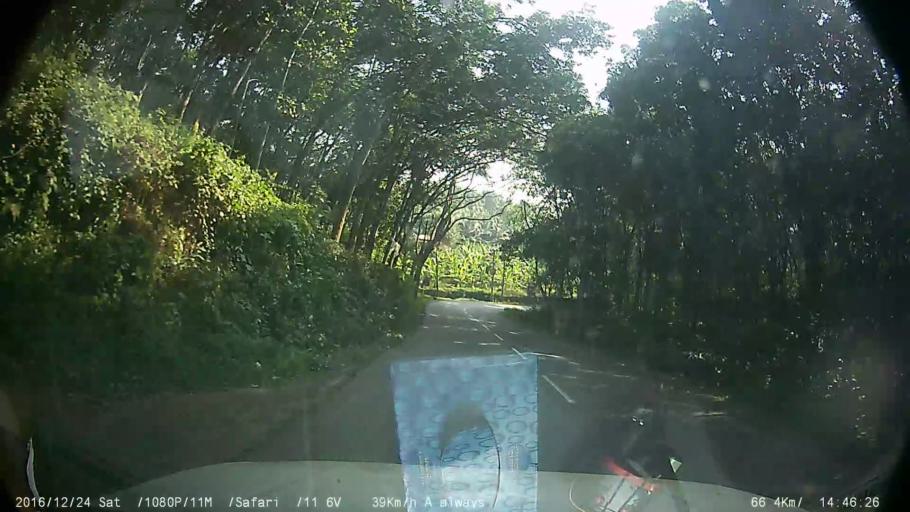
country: IN
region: Kerala
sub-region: Kottayam
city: Lalam
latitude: 9.7708
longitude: 76.7090
